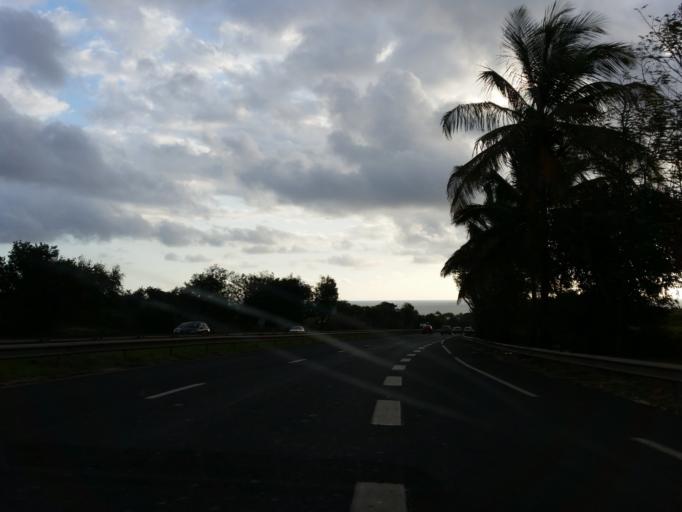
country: RE
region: Reunion
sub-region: Reunion
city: Saint-Pierre
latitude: -21.3297
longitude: 55.4704
